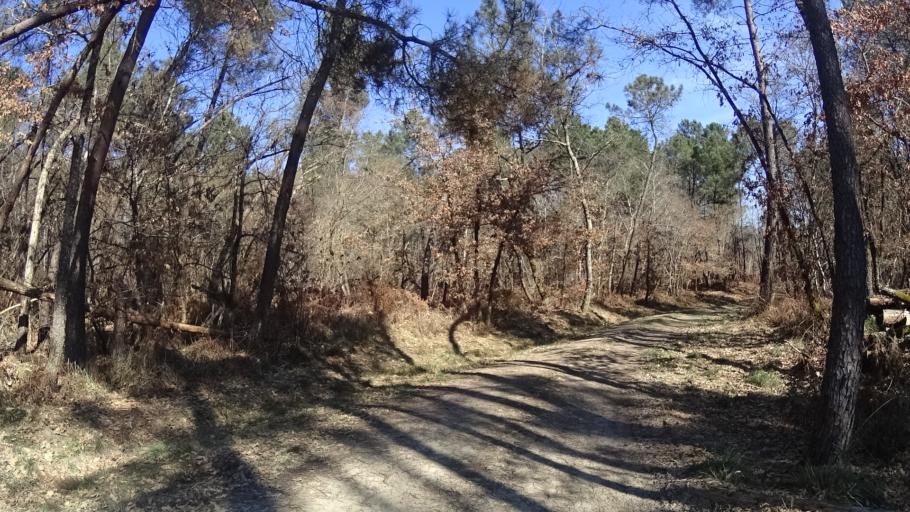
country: FR
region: Aquitaine
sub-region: Departement de la Dordogne
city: Riberac
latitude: 45.1861
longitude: 0.2960
